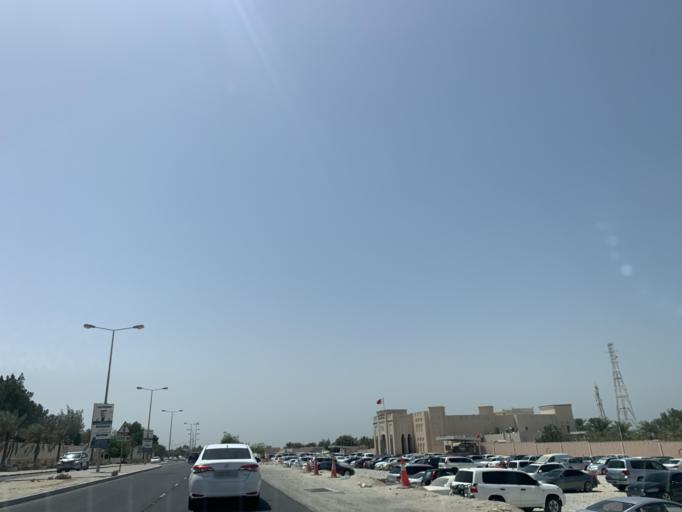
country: BH
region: Northern
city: Ar Rifa'
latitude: 26.1411
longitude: 50.5486
